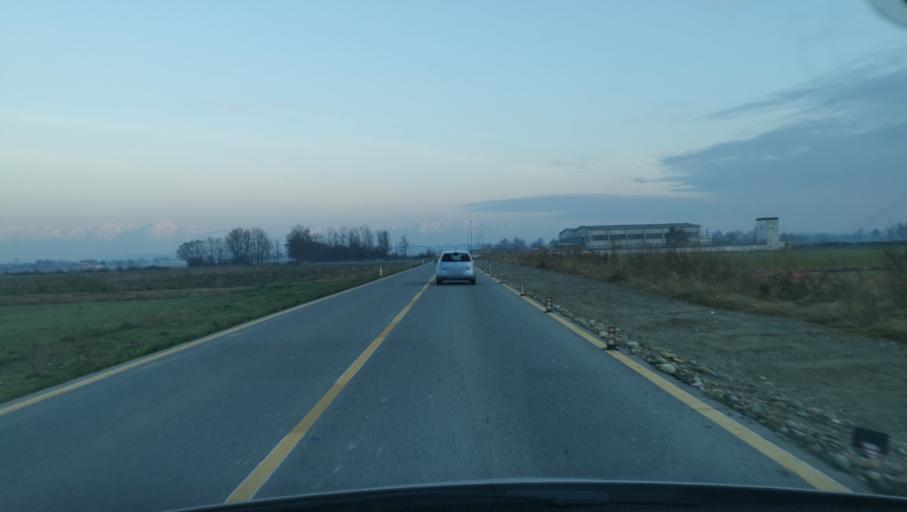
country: IT
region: Piedmont
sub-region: Provincia di Torino
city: Montanaro
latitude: 45.2591
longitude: 7.8920
